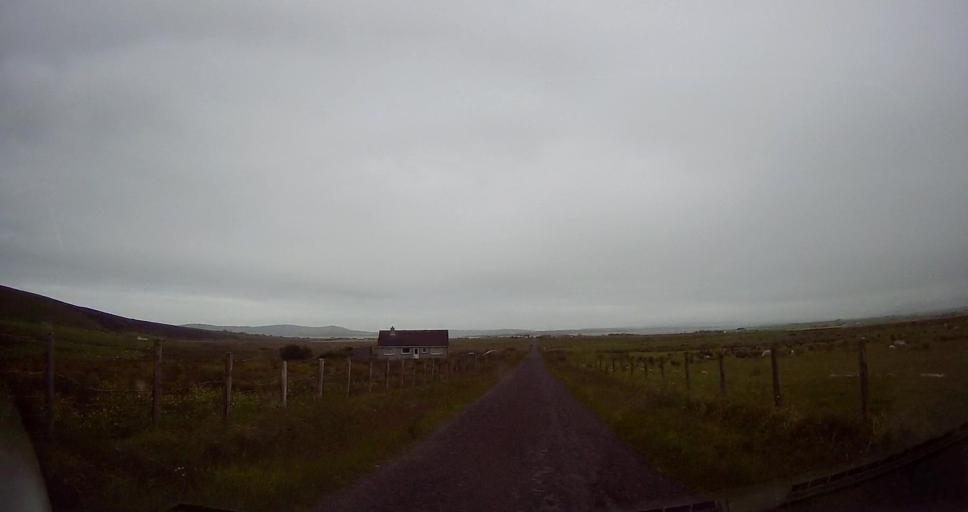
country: GB
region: Scotland
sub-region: Orkney Islands
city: Stromness
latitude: 58.9807
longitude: -3.1756
